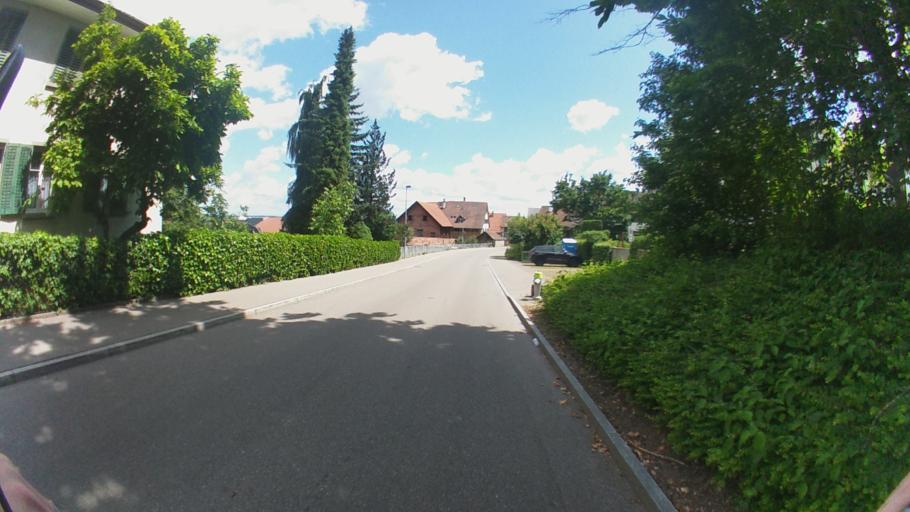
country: CH
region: Zurich
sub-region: Bezirk Dielsdorf
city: Dielsdorf
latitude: 47.4850
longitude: 8.4545
